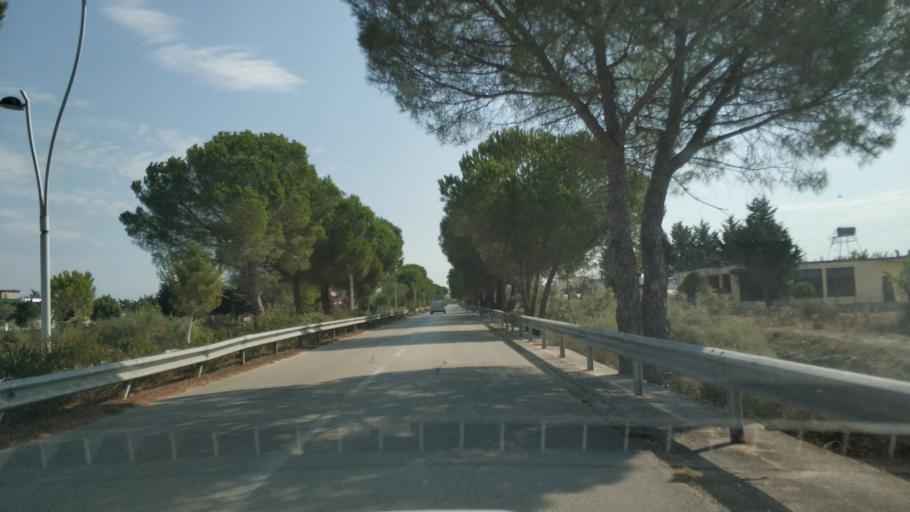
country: AL
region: Fier
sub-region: Rrethi i Lushnjes
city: Divjake
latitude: 40.9918
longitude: 19.5122
